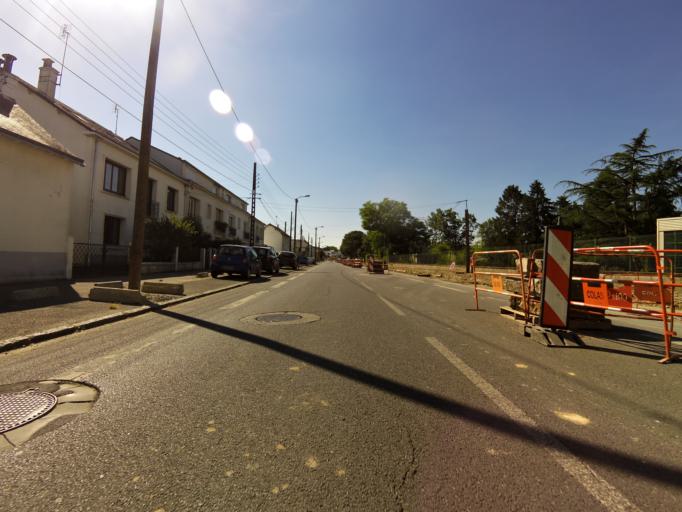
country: FR
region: Pays de la Loire
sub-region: Departement de la Loire-Atlantique
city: Nantes
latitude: 47.2519
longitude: -1.5729
